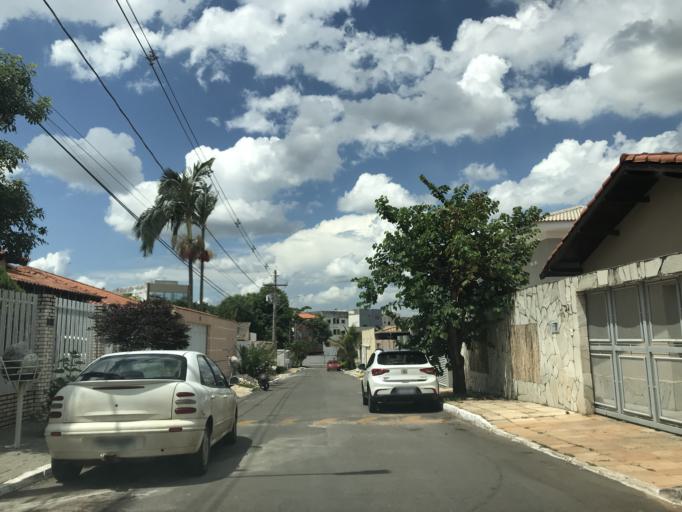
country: BR
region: Federal District
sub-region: Brasilia
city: Brasilia
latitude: -15.6828
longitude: -47.8342
